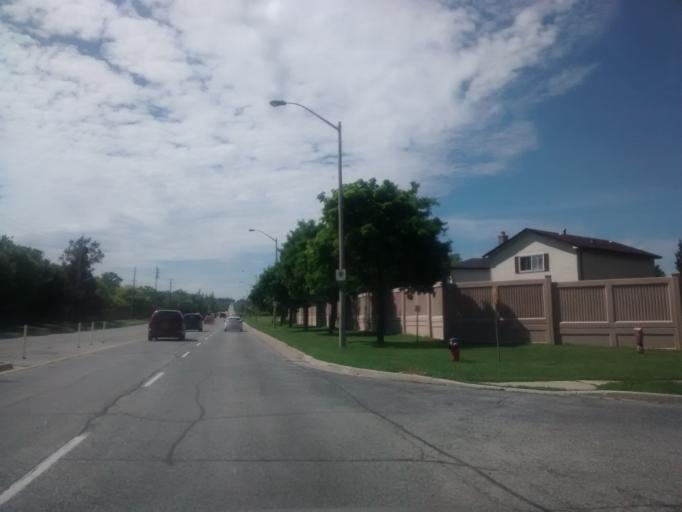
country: CA
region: Ontario
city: Burlington
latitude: 43.3759
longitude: -79.8371
